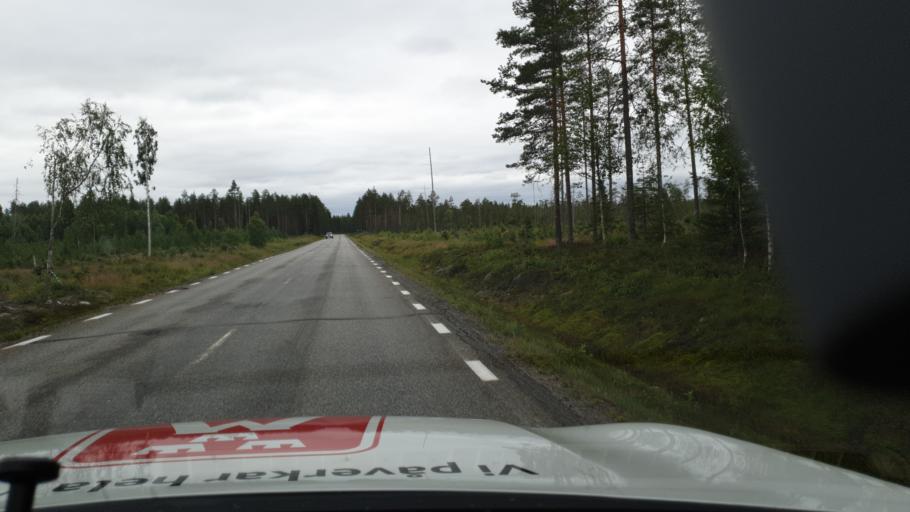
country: SE
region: Vaesterbotten
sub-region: Umea Kommun
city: Saevar
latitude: 64.0727
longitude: 20.4998
